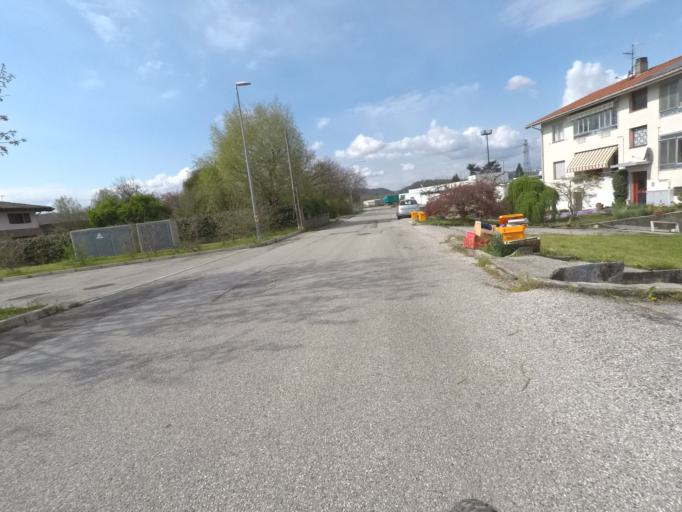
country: IT
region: Friuli Venezia Giulia
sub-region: Provincia di Udine
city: Artegna
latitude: 46.2352
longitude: 13.1504
